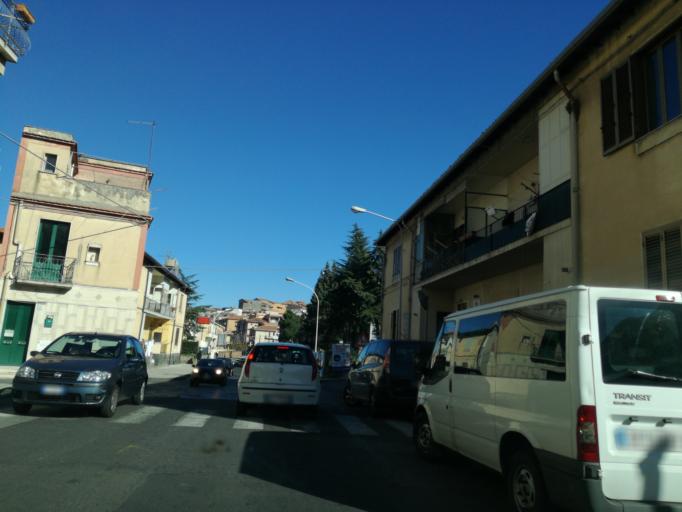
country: IT
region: Sicily
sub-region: Catania
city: Bronte
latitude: 37.7827
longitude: 14.8357
